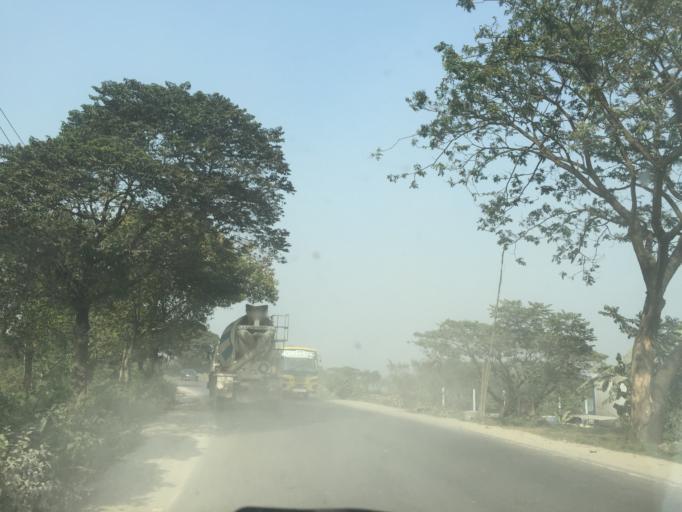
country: BD
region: Dhaka
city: Tungi
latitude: 23.8416
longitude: 90.3431
